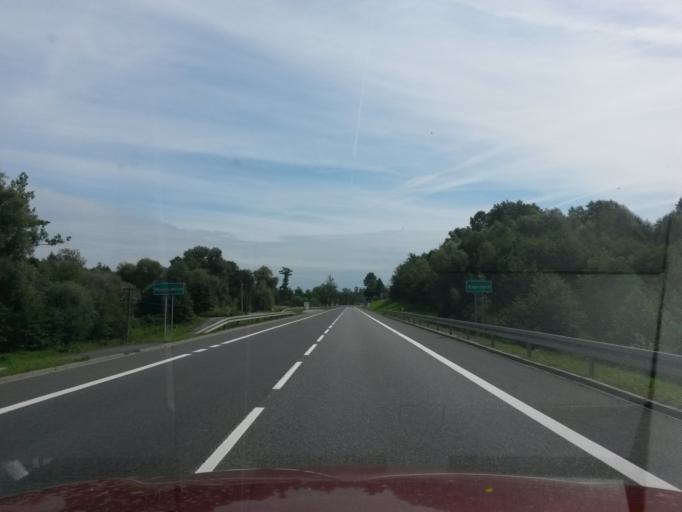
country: PL
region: Lesser Poland Voivodeship
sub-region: Powiat bochenski
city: Stanislawice
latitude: 49.9628
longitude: 20.3532
